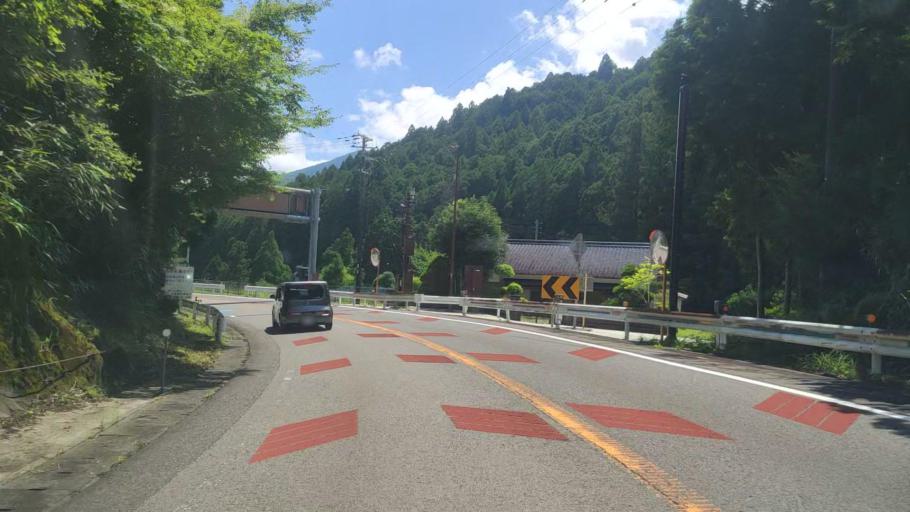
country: JP
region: Mie
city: Owase
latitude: 33.9864
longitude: 136.1083
